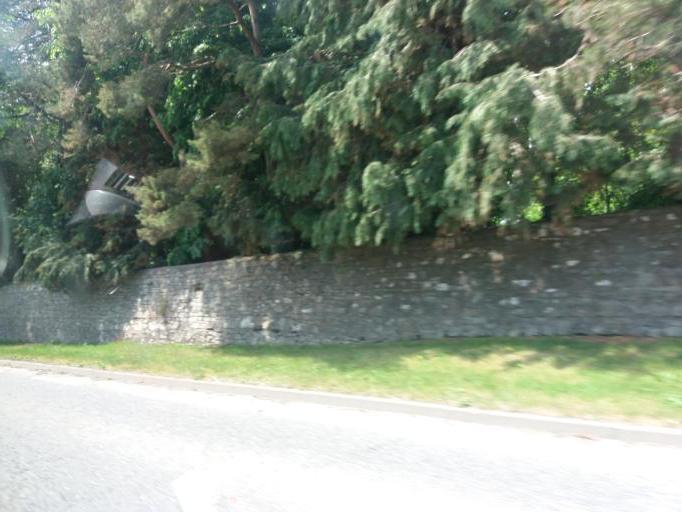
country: IE
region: Leinster
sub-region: An Mhi
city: Slane
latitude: 53.6941
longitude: -6.6083
